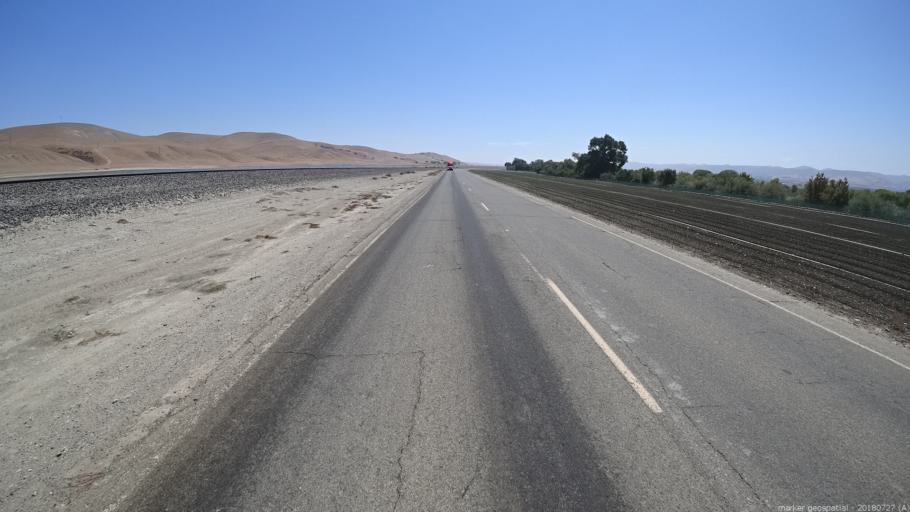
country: US
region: California
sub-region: Monterey County
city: King City
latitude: 36.0611
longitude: -120.9268
